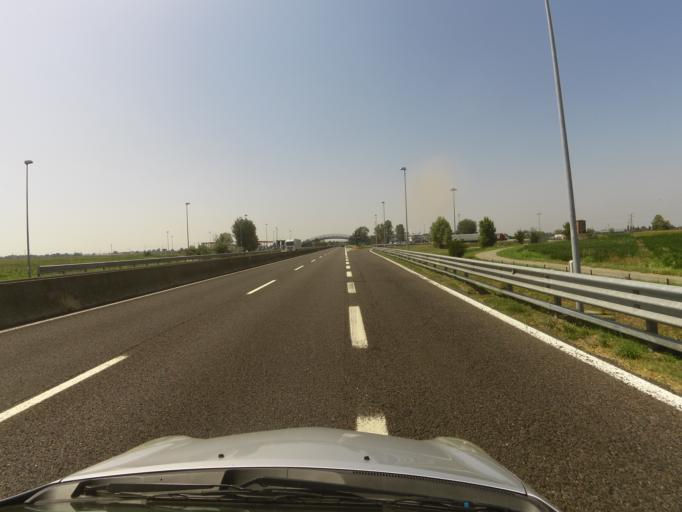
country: IT
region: Veneto
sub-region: Provincia di Rovigo
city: Costa di Rovigo
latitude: 45.0436
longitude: 11.7116
